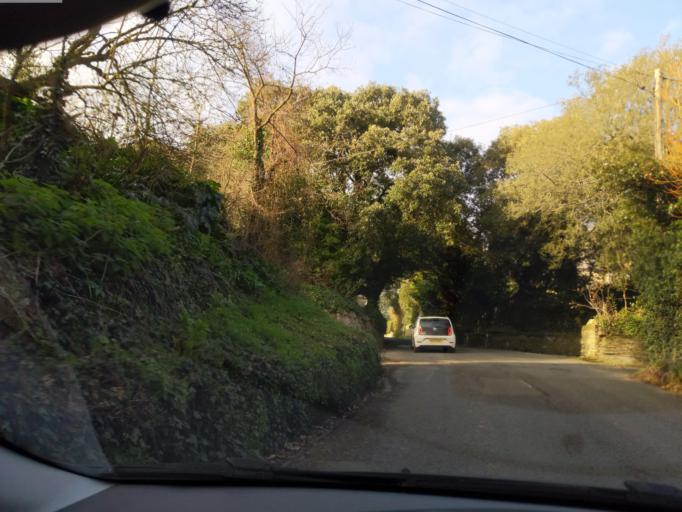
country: GB
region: England
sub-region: Cornwall
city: Padstow
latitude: 50.5121
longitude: -4.9417
